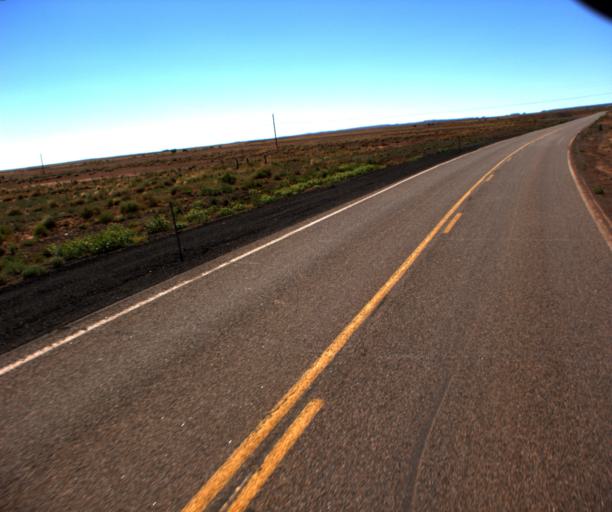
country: US
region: Arizona
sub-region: Coconino County
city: LeChee
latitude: 35.1529
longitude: -110.9002
